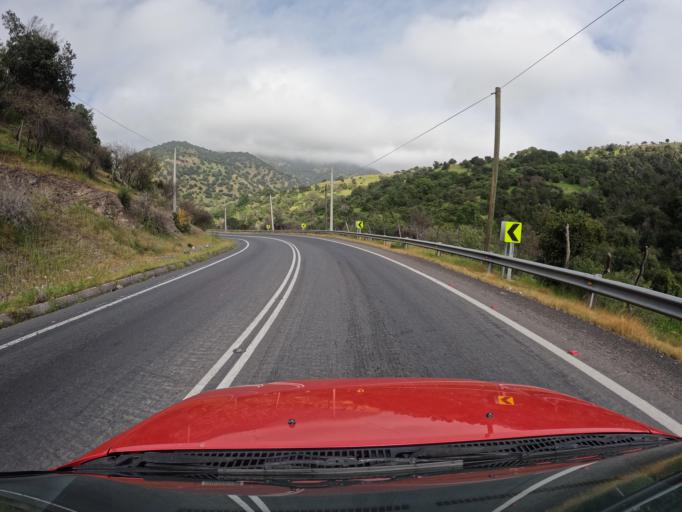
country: CL
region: Maule
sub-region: Provincia de Curico
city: Teno
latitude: -34.8157
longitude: -71.2042
